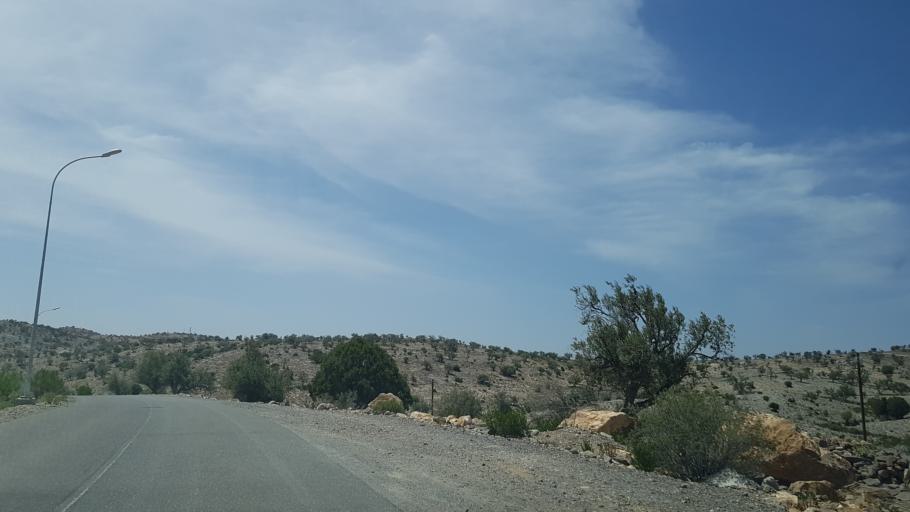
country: OM
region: Al Batinah
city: Bayt al `Awabi
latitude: 23.1219
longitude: 57.6128
